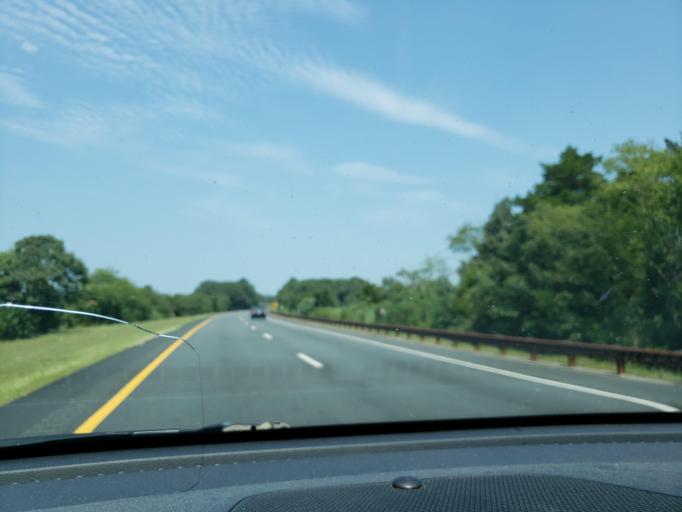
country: US
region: New Jersey
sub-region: Atlantic County
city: Somers Point
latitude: 39.3188
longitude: -74.6201
